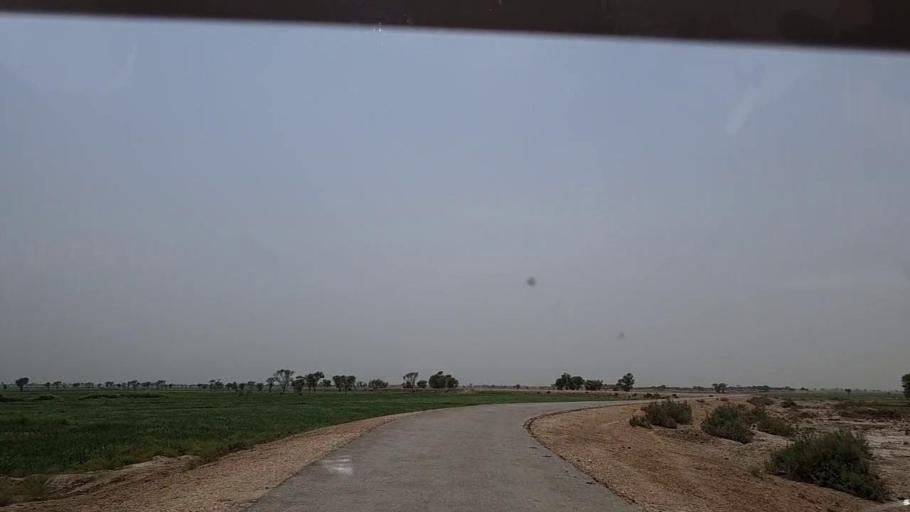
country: PK
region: Sindh
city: Khairpur Nathan Shah
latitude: 27.0223
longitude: 67.6678
